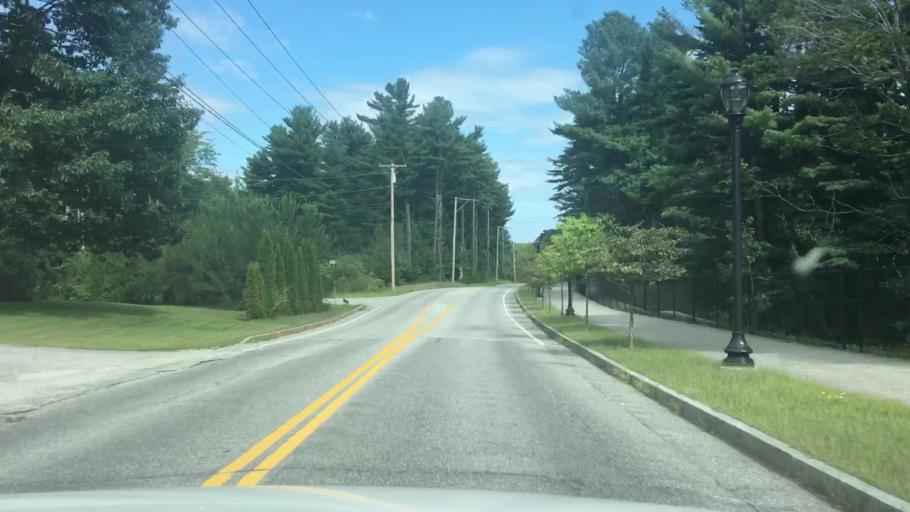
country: US
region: Maine
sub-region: Androscoggin County
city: Auburn
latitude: 44.0957
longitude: -70.2456
